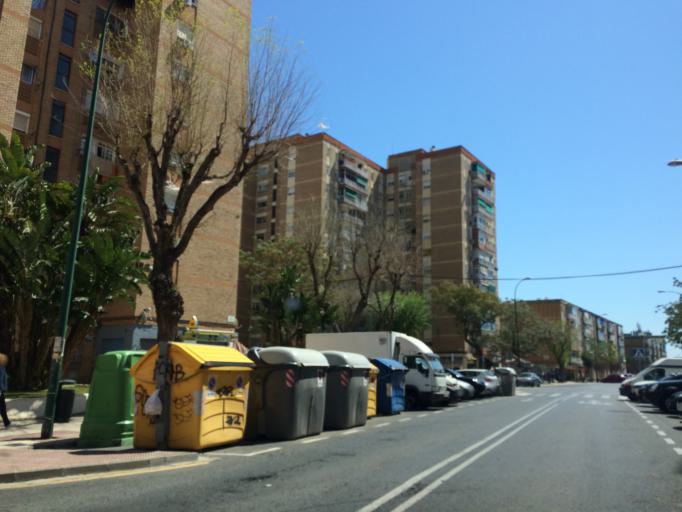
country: ES
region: Andalusia
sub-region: Provincia de Malaga
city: Malaga
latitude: 36.6914
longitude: -4.4541
